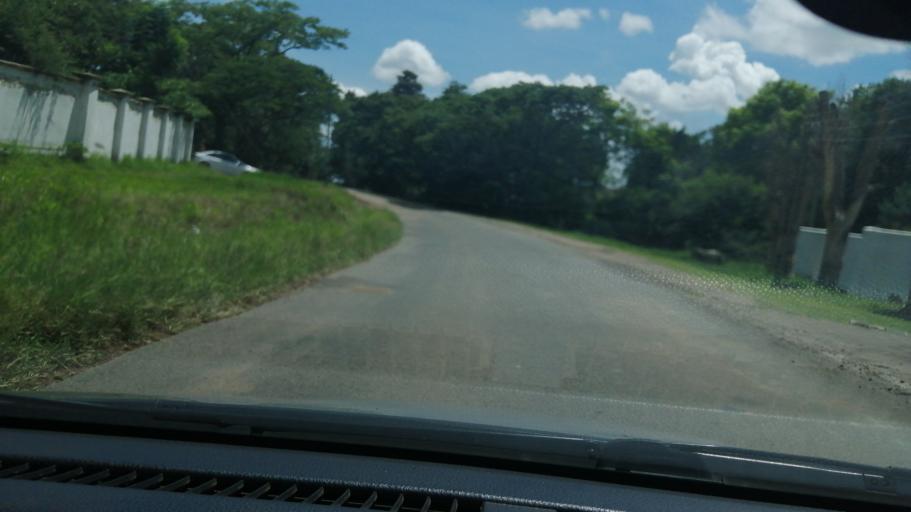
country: ZW
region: Harare
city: Harare
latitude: -17.7725
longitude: 31.0965
